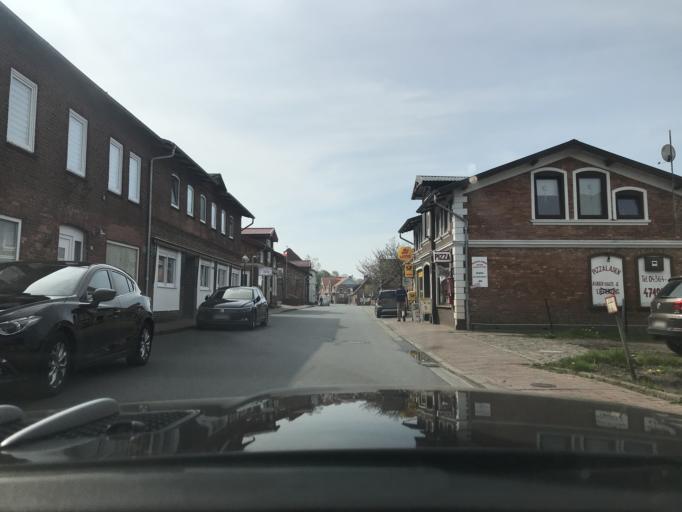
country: DE
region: Schleswig-Holstein
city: Grube
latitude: 54.2321
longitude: 11.0361
